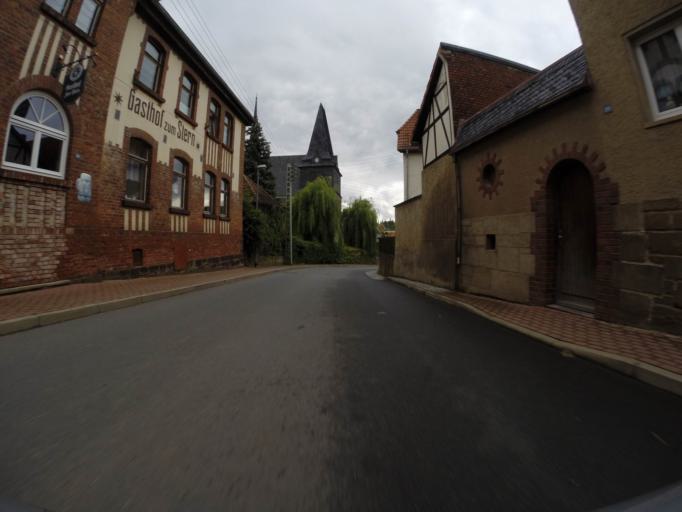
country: DE
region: Thuringia
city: Nausnitz
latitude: 50.9605
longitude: 11.7189
